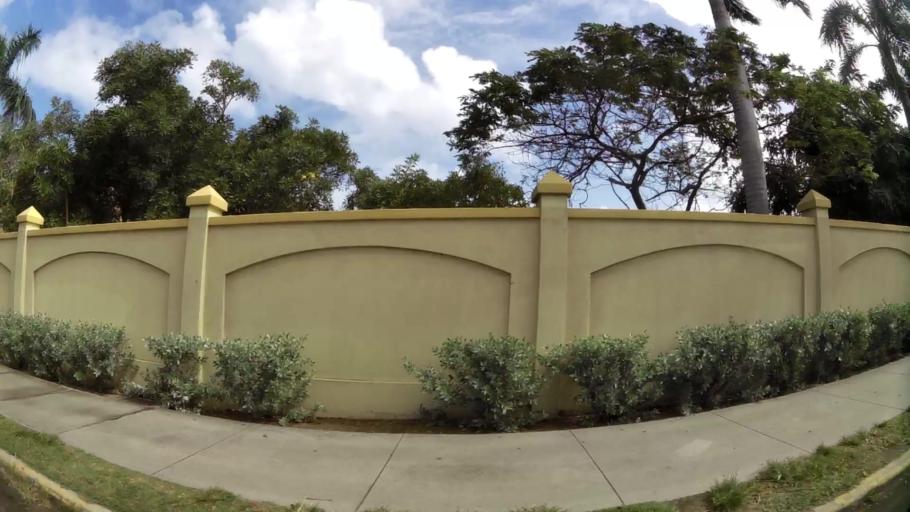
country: KN
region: Saint Peter Basseterre
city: Monkey Hill
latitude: 17.2907
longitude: -62.6858
